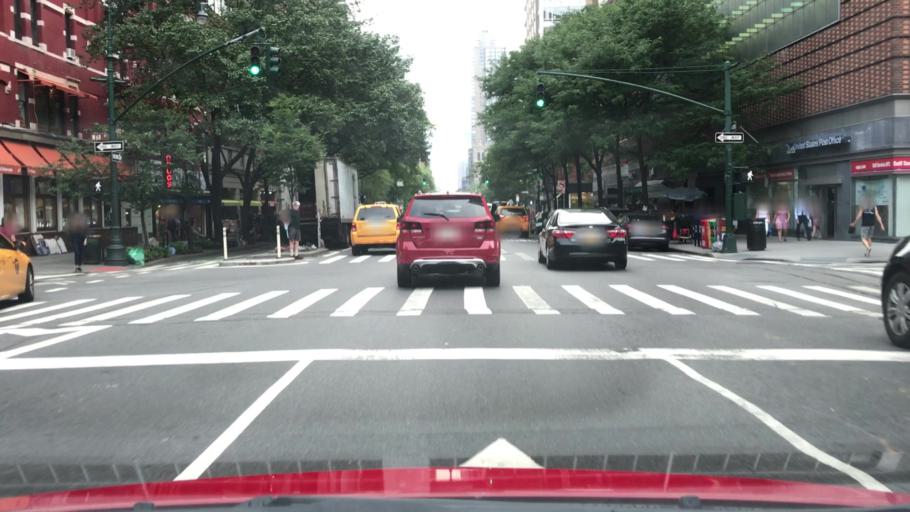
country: US
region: New York
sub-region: New York County
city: Manhattan
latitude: 40.7750
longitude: -73.9806
